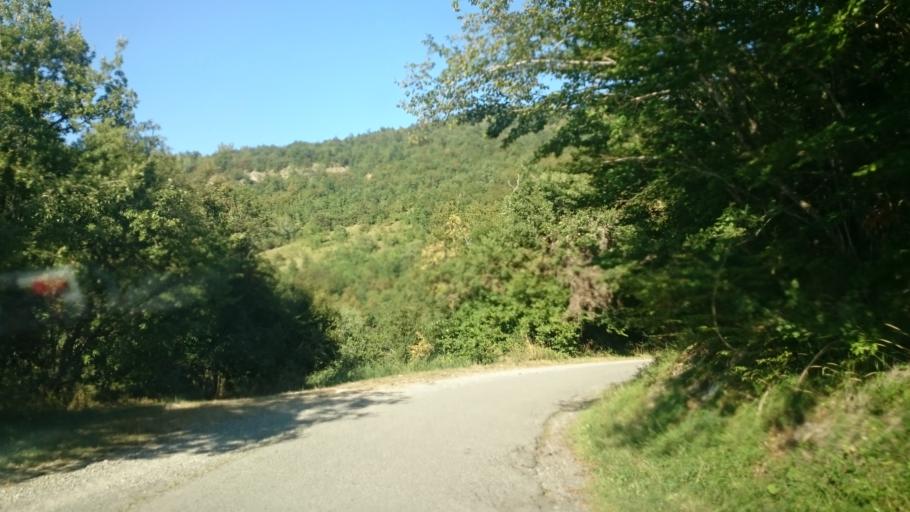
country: IT
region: Emilia-Romagna
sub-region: Provincia di Reggio Emilia
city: Villa Minozzo
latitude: 44.3168
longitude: 10.4709
